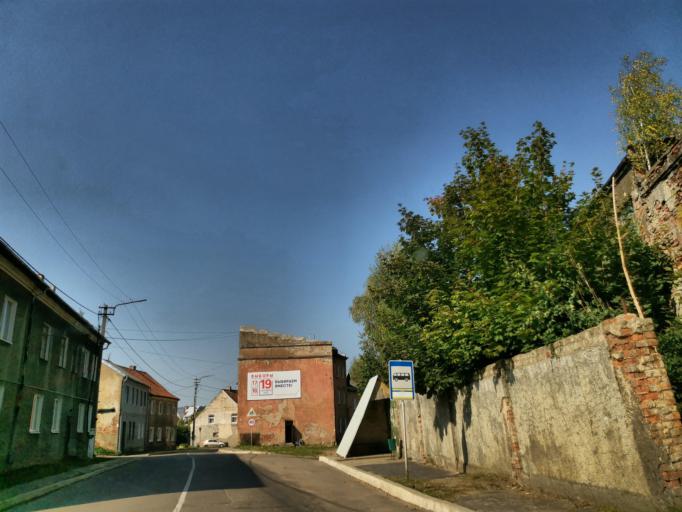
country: RU
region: Kaliningrad
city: Neman
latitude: 55.0348
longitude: 22.0369
